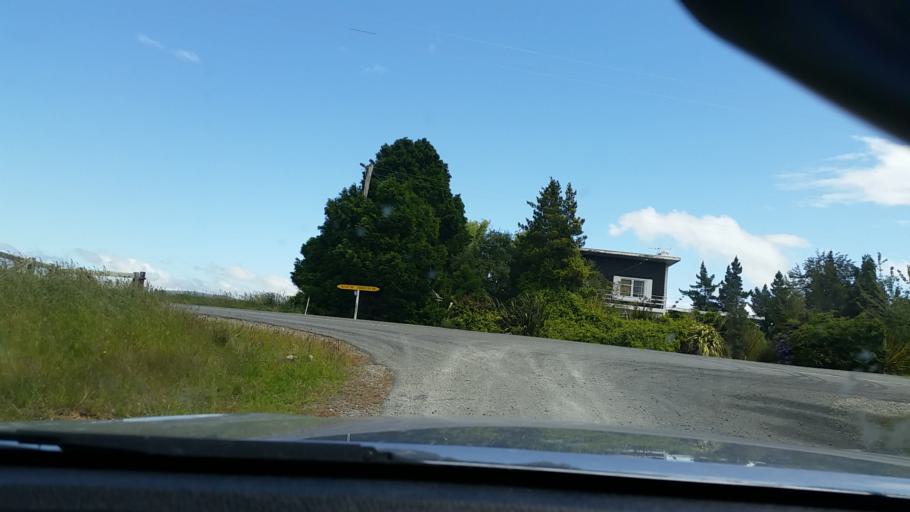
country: NZ
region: Southland
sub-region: Southland District
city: Winton
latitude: -45.8080
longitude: 168.5826
